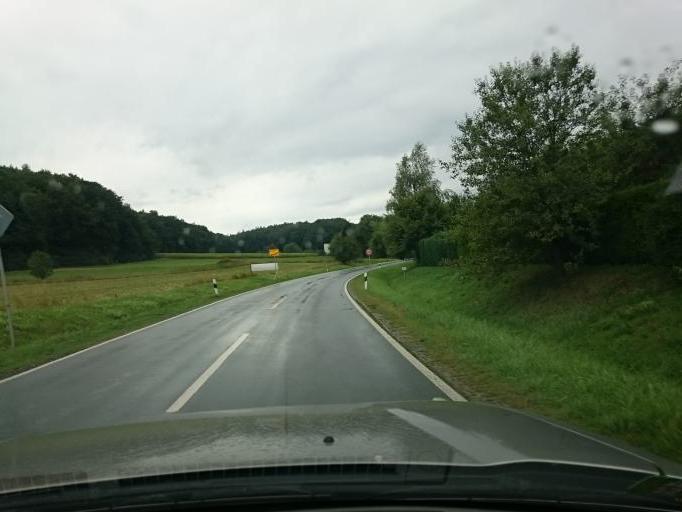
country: DE
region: Bavaria
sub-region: Upper Franconia
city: Obertrubach
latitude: 49.6815
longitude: 11.4120
